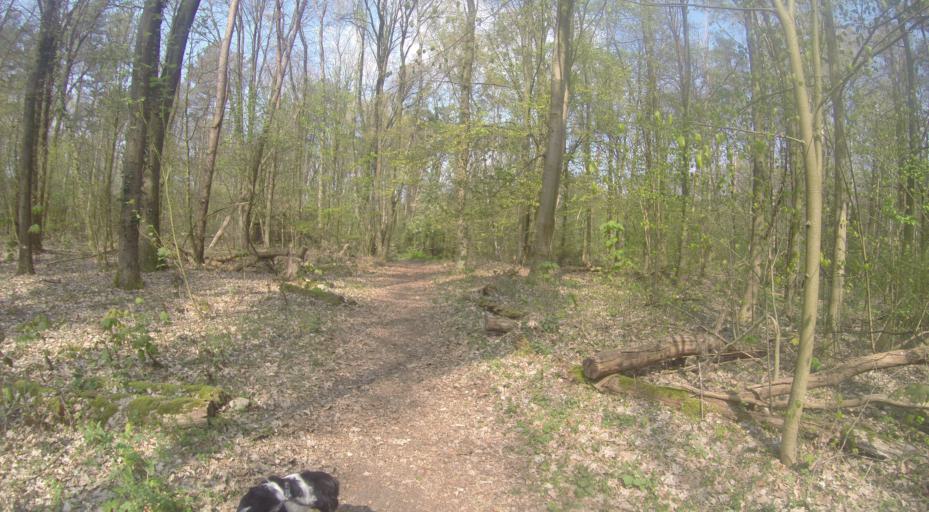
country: NL
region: Gelderland
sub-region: Gemeente Doetinchem
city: Doetinchem
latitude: 51.9507
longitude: 6.3244
